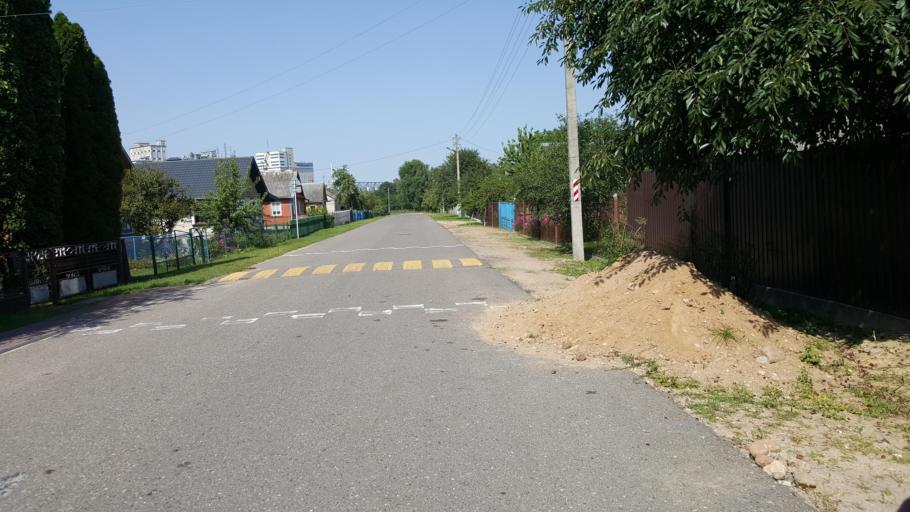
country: BY
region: Brest
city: Zhabinka
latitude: 52.1984
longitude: 24.0232
